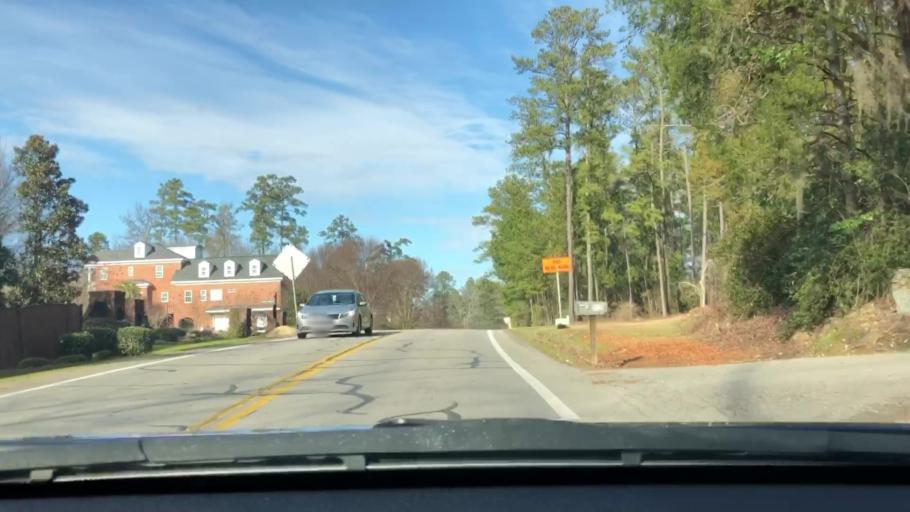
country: US
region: South Carolina
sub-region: Lexington County
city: Irmo
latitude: 34.0601
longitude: -81.1802
